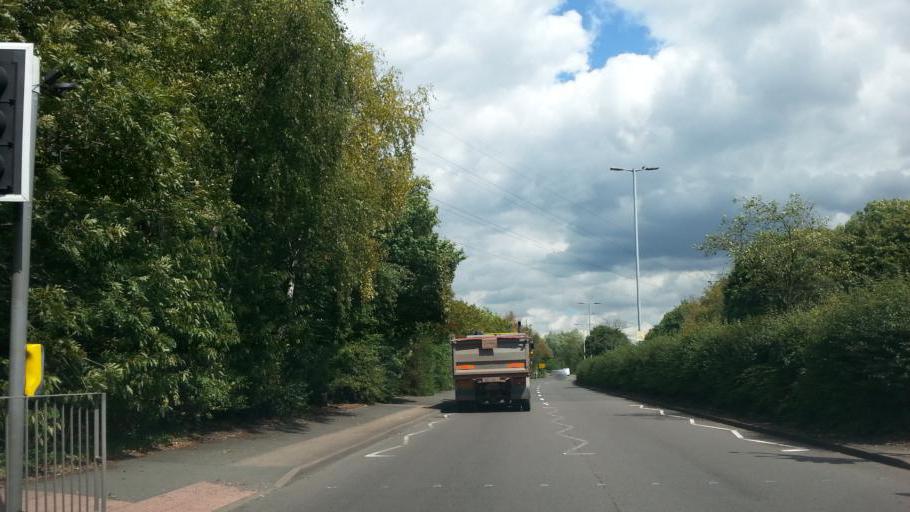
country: GB
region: England
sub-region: Wolverhampton
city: Bilston
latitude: 52.5526
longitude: -2.0969
